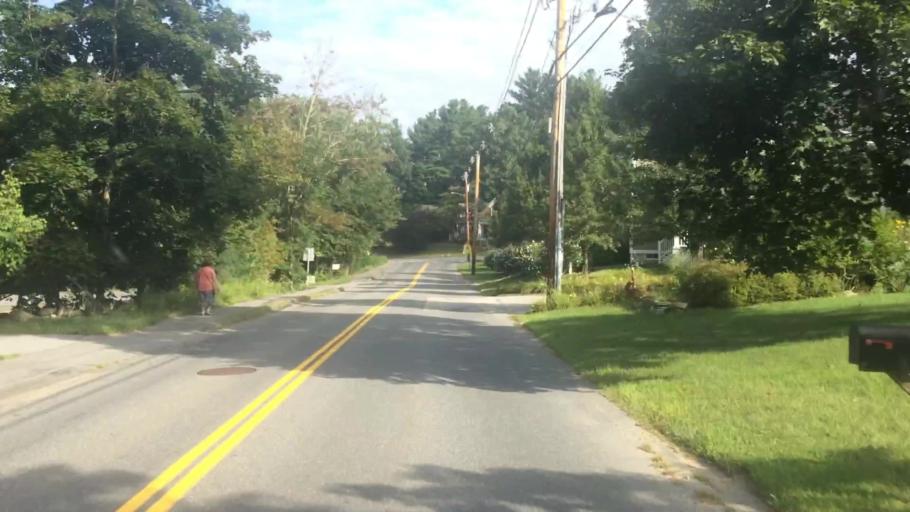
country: US
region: Massachusetts
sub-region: Middlesex County
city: Acton
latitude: 42.4737
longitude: -71.4591
